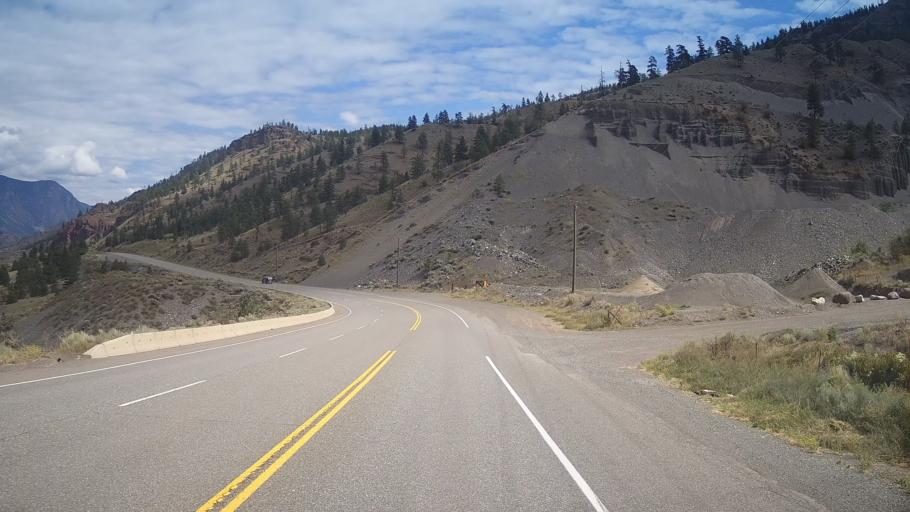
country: CA
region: British Columbia
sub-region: Thompson-Nicola Regional District
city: Ashcroft
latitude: 50.2941
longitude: -121.3936
